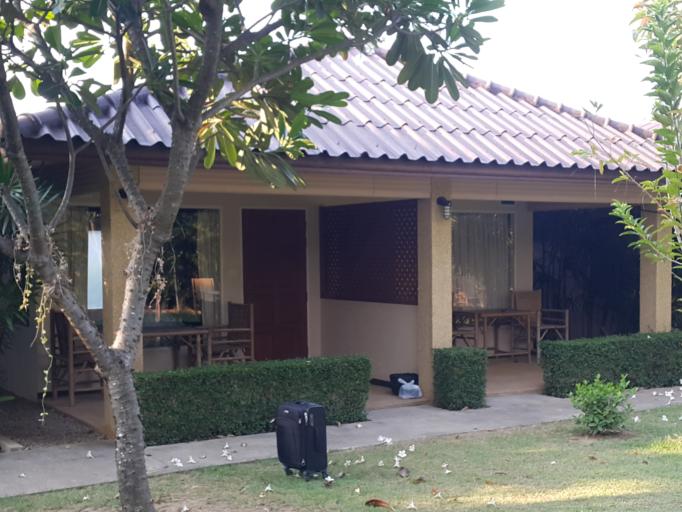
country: TH
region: Kanchanaburi
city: Kanchanaburi
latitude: 14.0327
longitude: 99.5228
